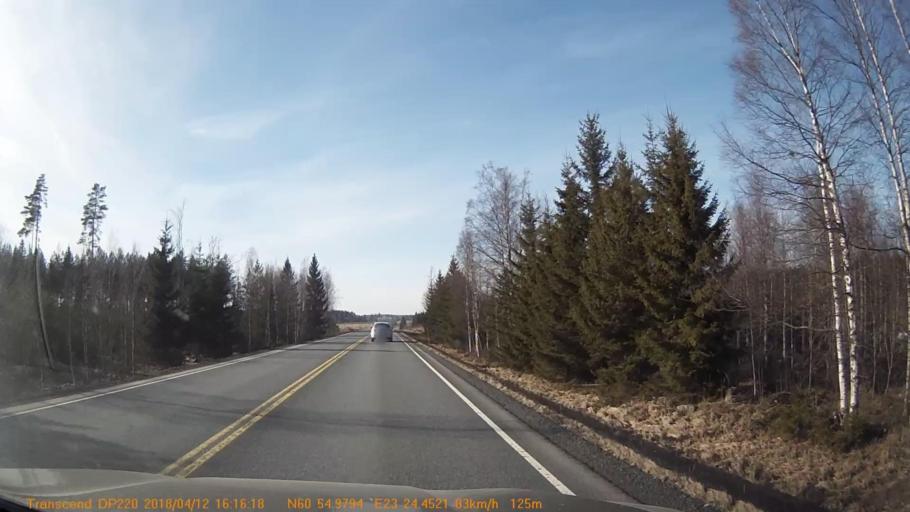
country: FI
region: Haeme
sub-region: Forssa
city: Humppila
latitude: 60.9165
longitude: 23.4072
